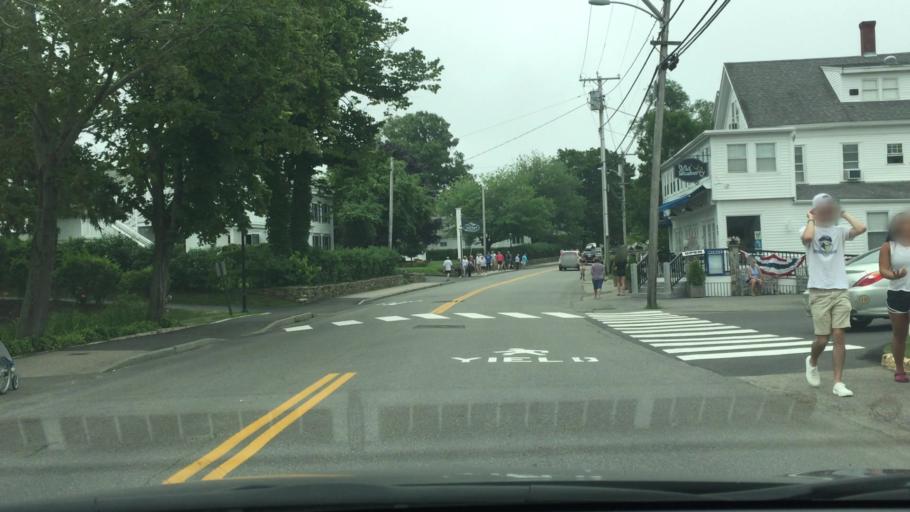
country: US
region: Maine
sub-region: York County
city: Ogunquit
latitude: 43.2471
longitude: -70.5977
